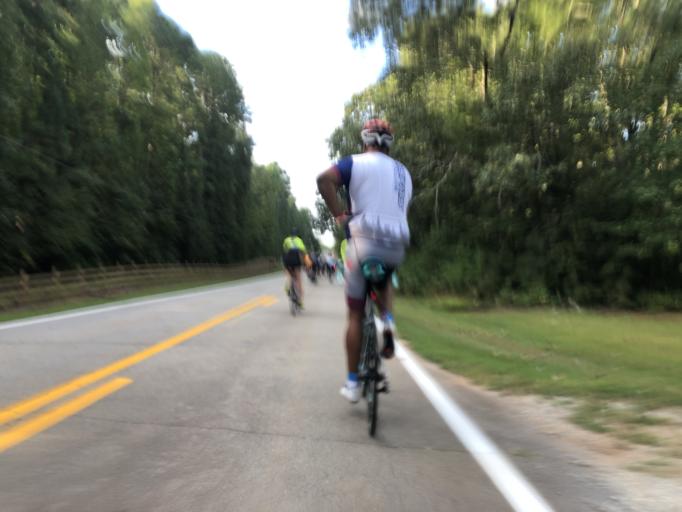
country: US
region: Georgia
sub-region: Fulton County
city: Palmetto
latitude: 33.5763
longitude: -84.6493
